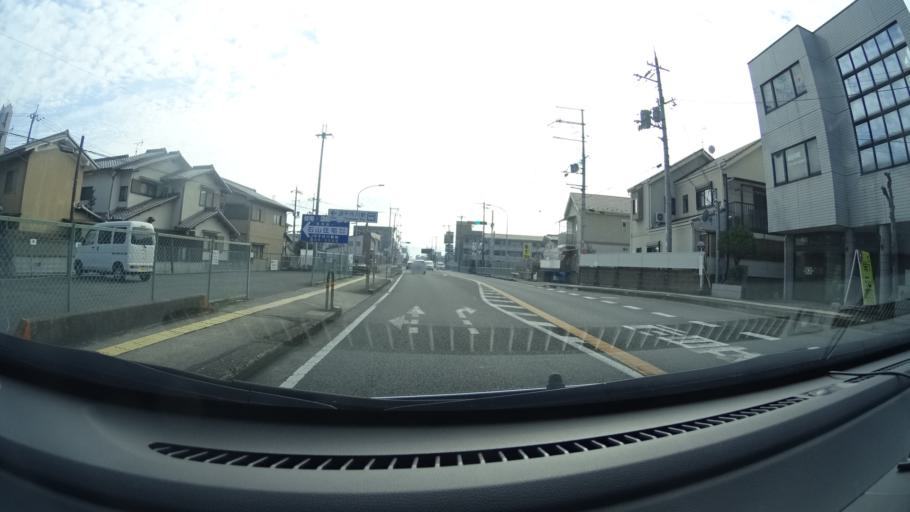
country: JP
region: Kyoto
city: Kameoka
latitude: 35.0491
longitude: 135.5451
